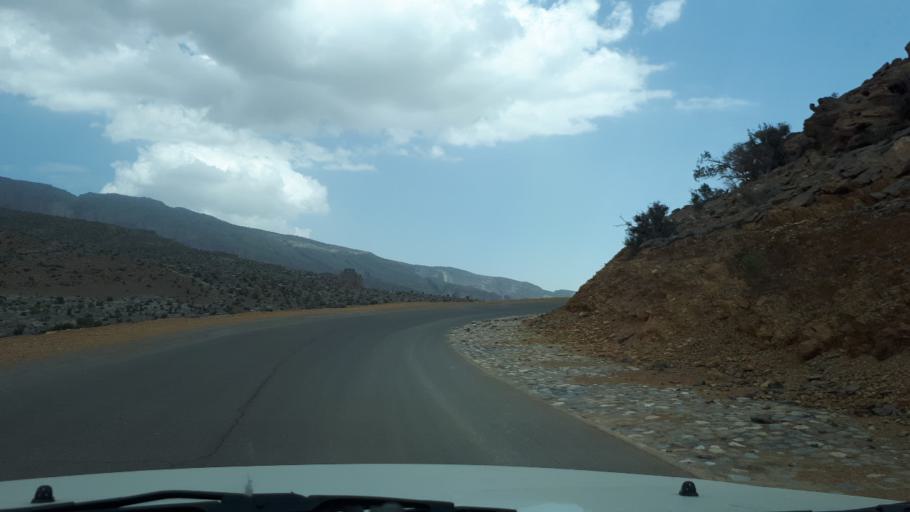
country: OM
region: Muhafazat ad Dakhiliyah
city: Bahla'
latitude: 23.2238
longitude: 57.2049
